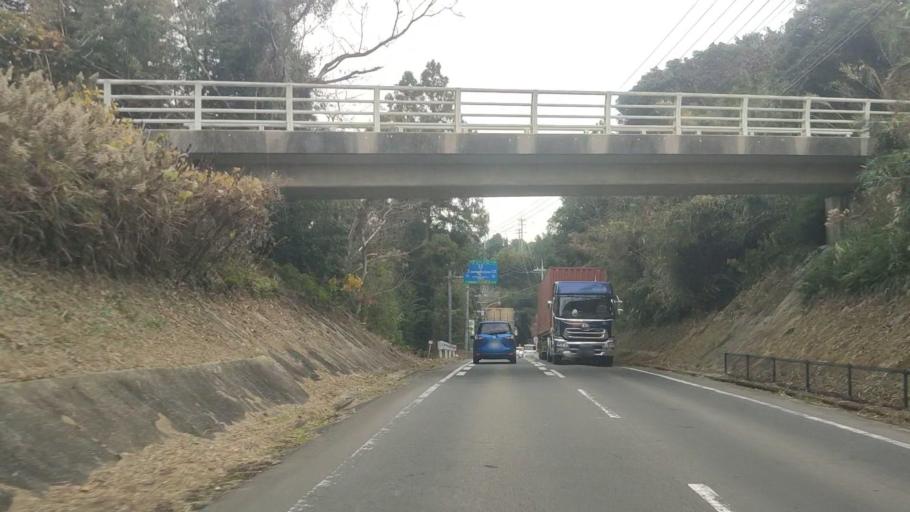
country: JP
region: Nagasaki
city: Shimabara
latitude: 32.8490
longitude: 130.2288
